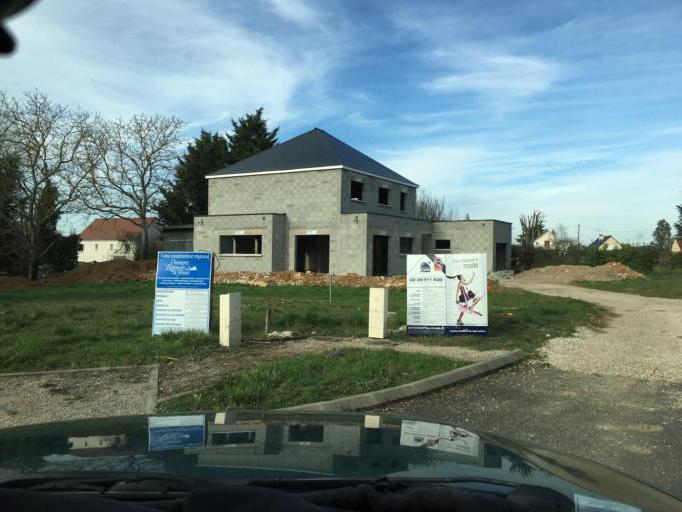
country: FR
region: Centre
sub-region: Departement du Loiret
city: Beaugency
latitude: 47.7828
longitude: 1.6146
